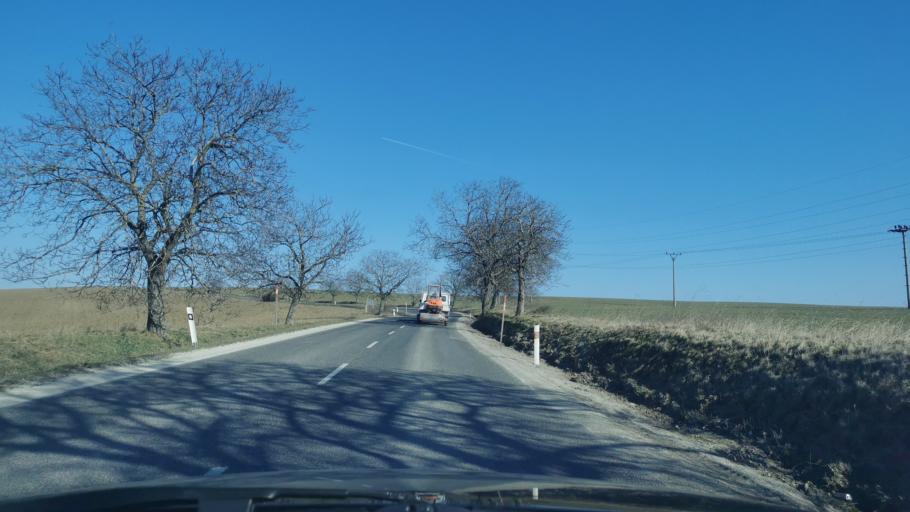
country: SK
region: Trnavsky
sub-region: Okres Senica
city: Senica
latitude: 48.7319
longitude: 17.4193
